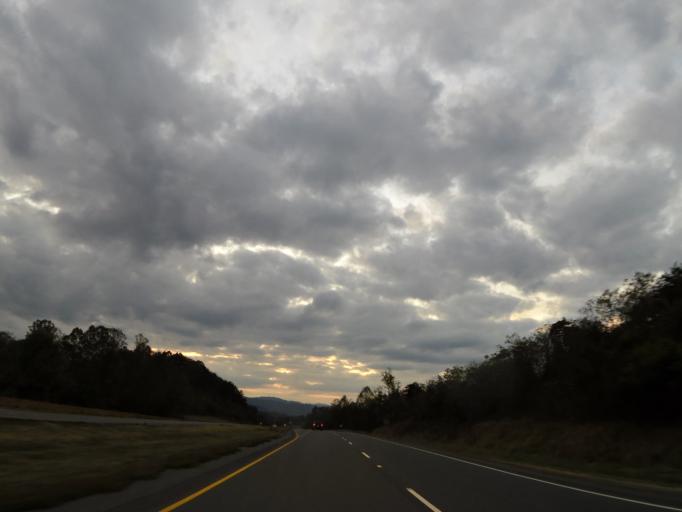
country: US
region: North Carolina
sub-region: Madison County
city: Marshall
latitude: 35.7849
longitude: -82.6431
